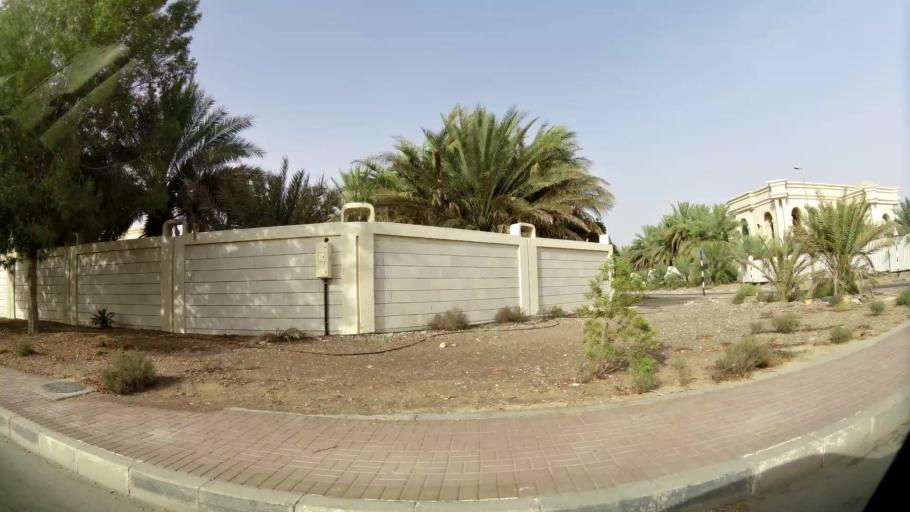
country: AE
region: Abu Dhabi
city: Al Ain
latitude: 24.2172
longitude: 55.6507
